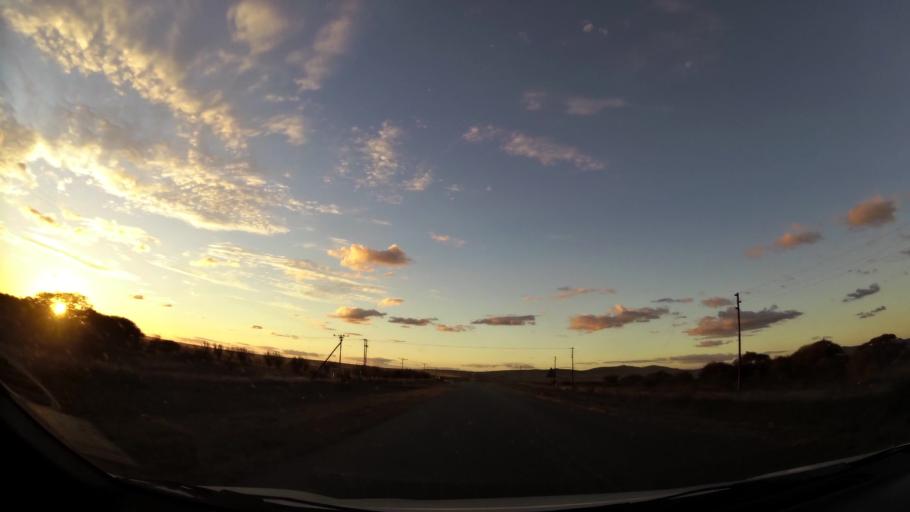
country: ZA
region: Limpopo
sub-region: Capricorn District Municipality
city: Polokwane
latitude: -23.7623
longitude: 29.4742
